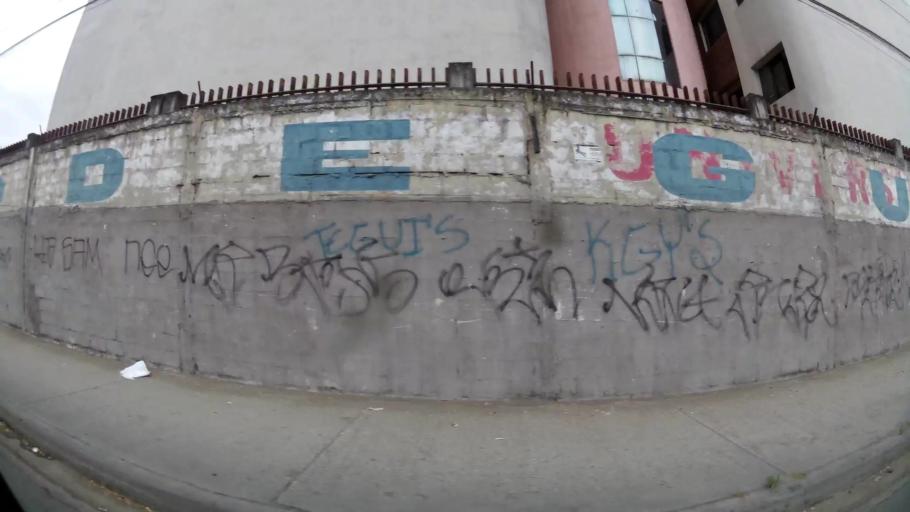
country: EC
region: Guayas
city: Guayaquil
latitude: -2.1449
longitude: -79.9103
